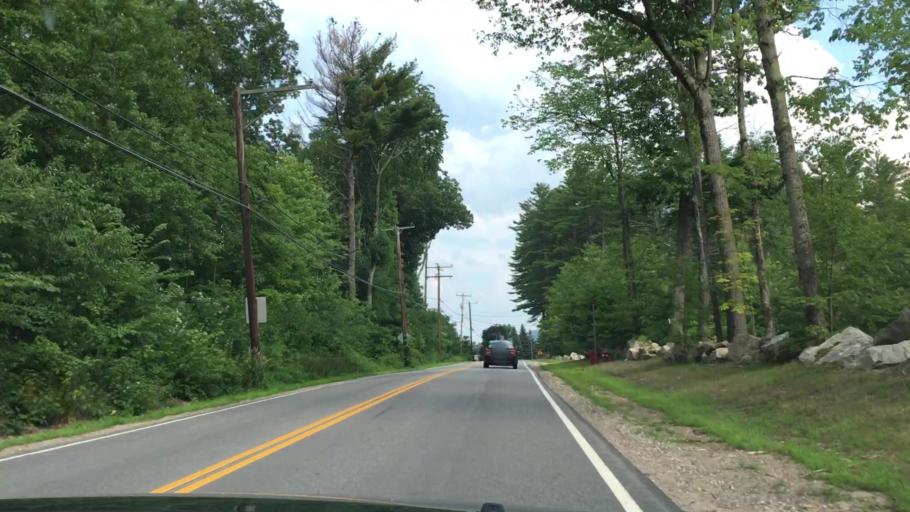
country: US
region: New Hampshire
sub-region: Belknap County
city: Gilford
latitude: 43.6006
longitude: -71.4351
